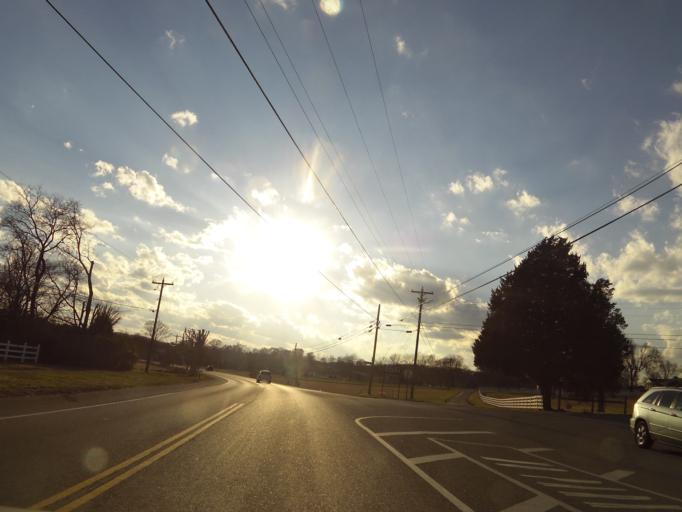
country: US
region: Tennessee
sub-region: Smith County
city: Carthage
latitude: 36.2587
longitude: -86.0919
